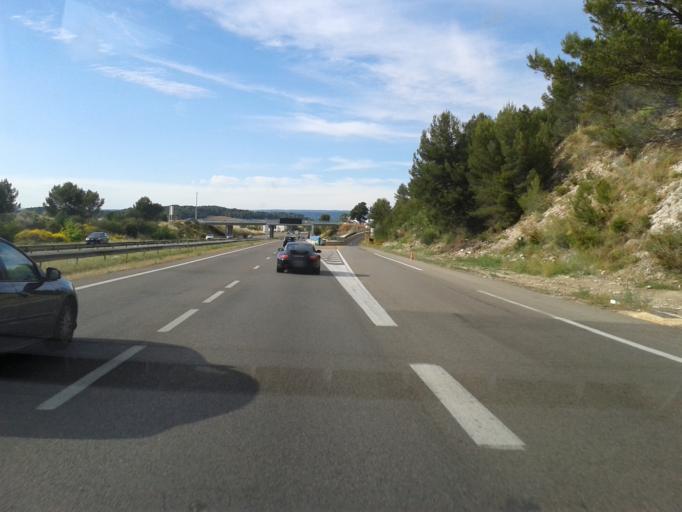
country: FR
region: Provence-Alpes-Cote d'Azur
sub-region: Departement des Bouches-du-Rhone
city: Bouc-Bel-Air
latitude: 43.4685
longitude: 5.4074
